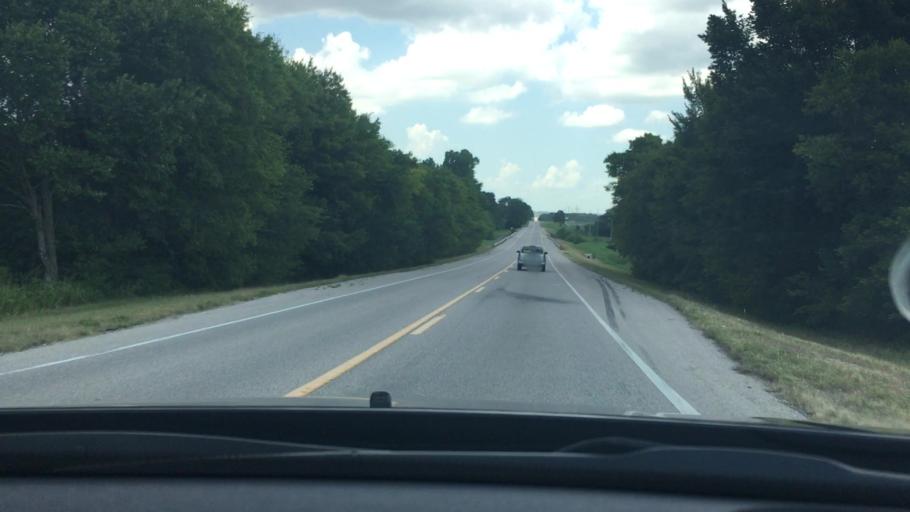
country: US
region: Oklahoma
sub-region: Pontotoc County
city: Ada
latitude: 34.6827
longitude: -96.6349
